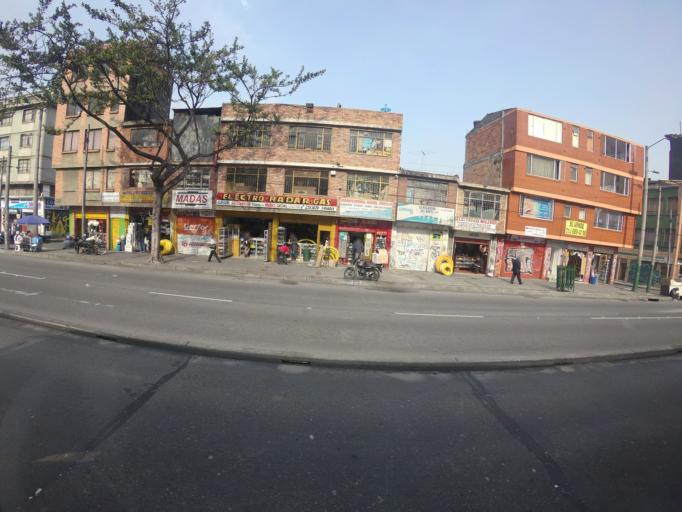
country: CO
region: Bogota D.C.
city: Bogota
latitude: 4.6483
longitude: -74.0650
